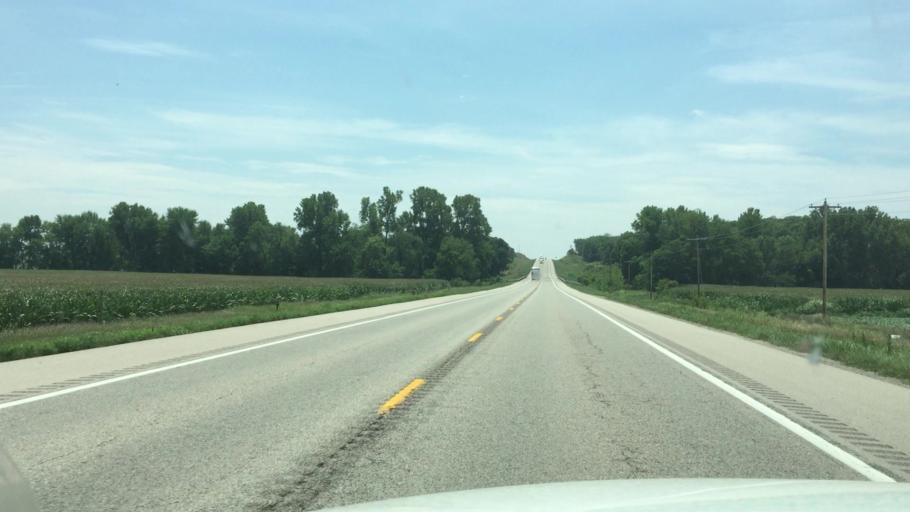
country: US
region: Kansas
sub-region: Jackson County
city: Holton
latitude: 39.6320
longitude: -95.7311
